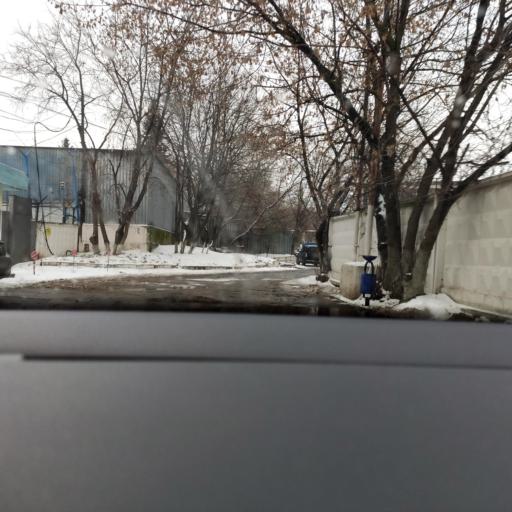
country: RU
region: Moscow
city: Metrogorodok
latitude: 55.8235
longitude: 37.7798
